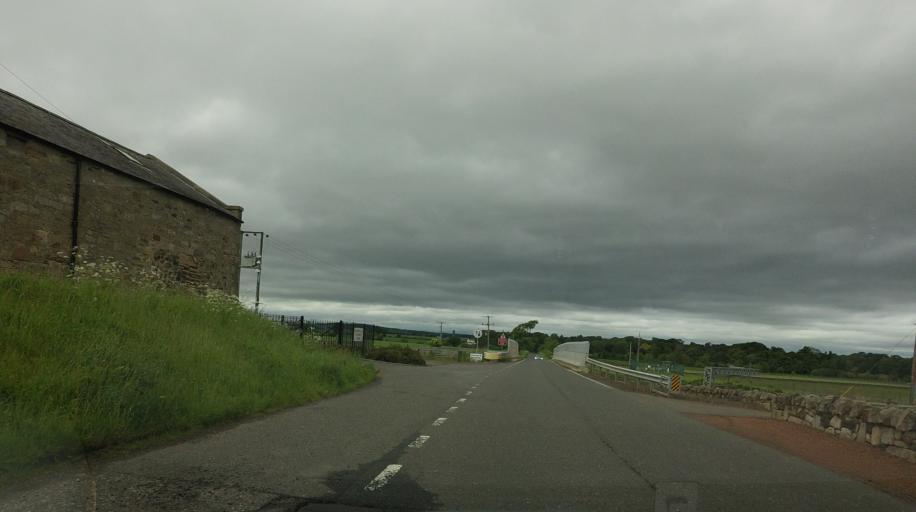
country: GB
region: Scotland
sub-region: Edinburgh
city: Ratho
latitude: 55.9271
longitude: -3.3438
